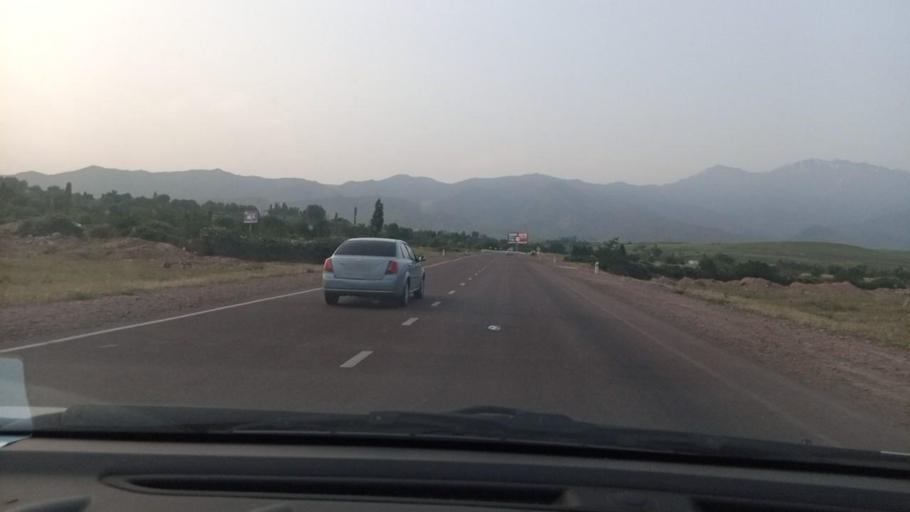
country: UZ
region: Toshkent
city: Angren
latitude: 41.0470
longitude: 70.1586
